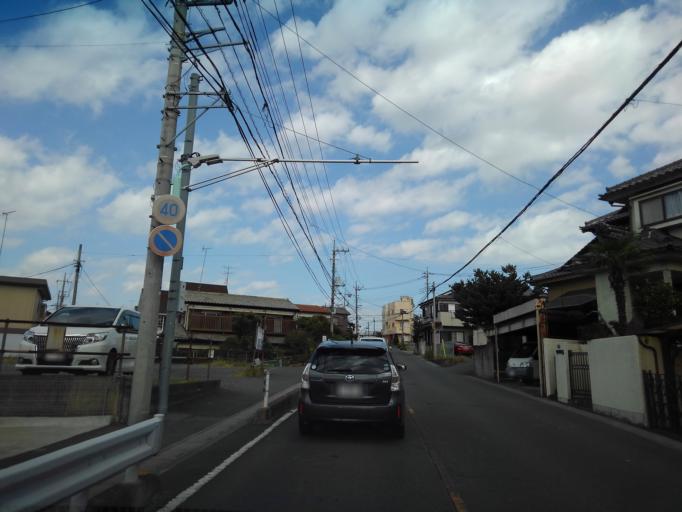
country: JP
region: Saitama
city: Tokorozawa
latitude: 35.7771
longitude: 139.4723
